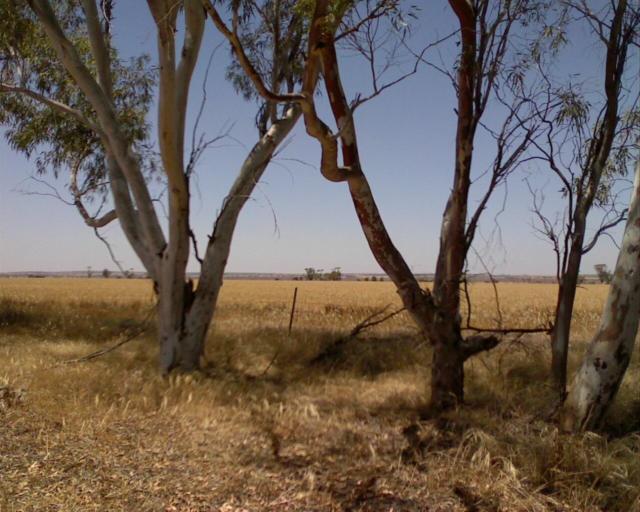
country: AU
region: Western Australia
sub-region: Wongan-Ballidu
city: Wongan Hills
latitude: -30.4554
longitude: 117.5270
